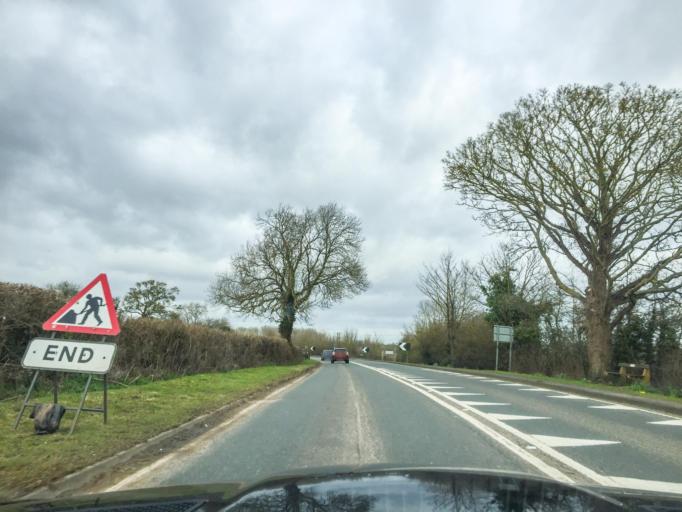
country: GB
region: England
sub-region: Warwickshire
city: Shipston on Stour
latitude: 52.0694
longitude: -1.6200
